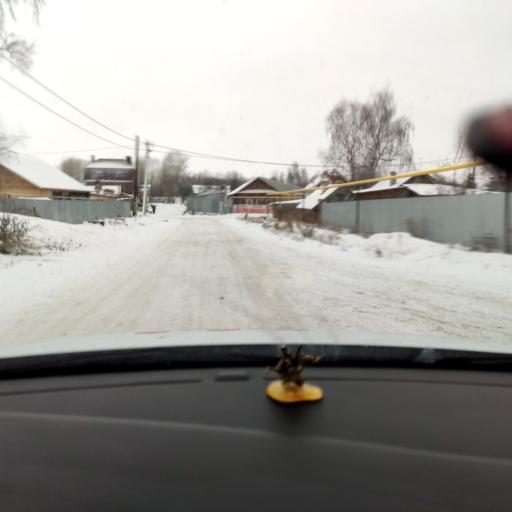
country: RU
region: Tatarstan
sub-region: Gorod Kazan'
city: Kazan
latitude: 55.7393
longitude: 49.0970
